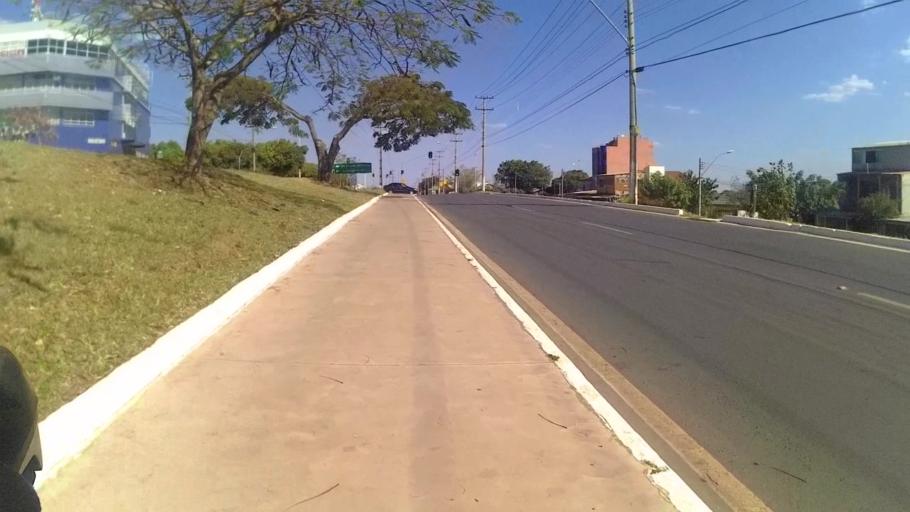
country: BR
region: Federal District
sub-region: Brasilia
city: Brasilia
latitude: -15.7779
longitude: -47.7820
